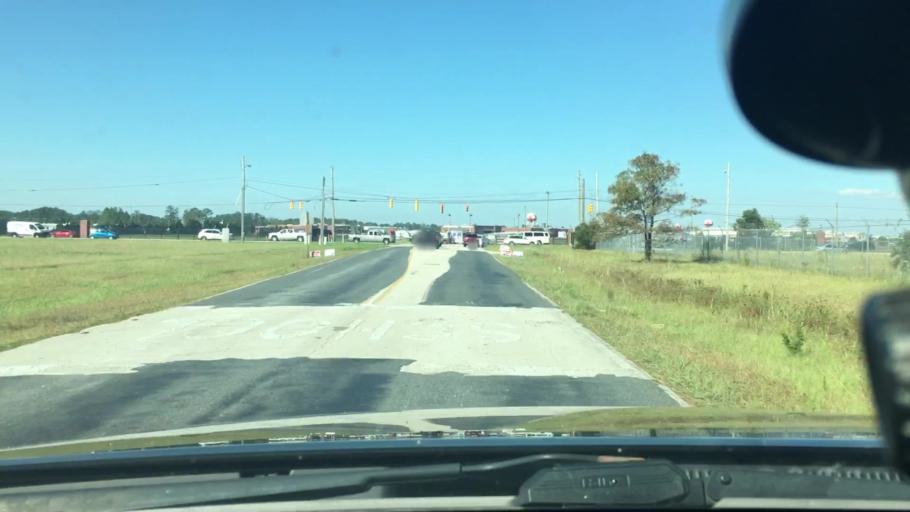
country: US
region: North Carolina
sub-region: Craven County
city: Havelock
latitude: 34.8814
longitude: -76.9007
